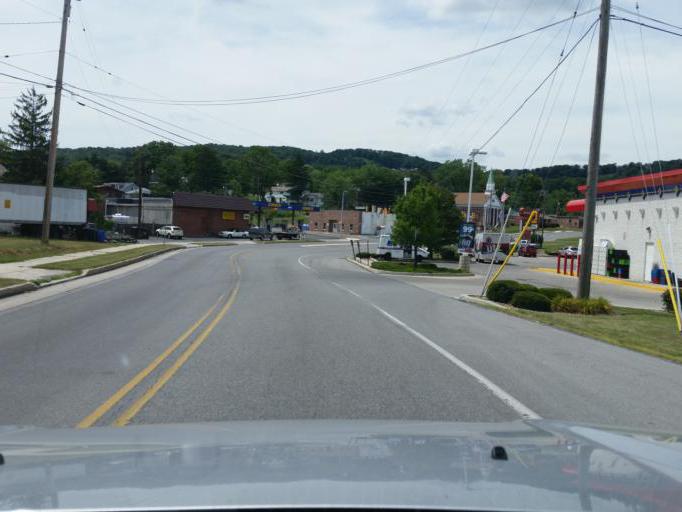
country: US
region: Pennsylvania
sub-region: Blair County
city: Altoona
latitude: 40.5345
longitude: -78.4007
